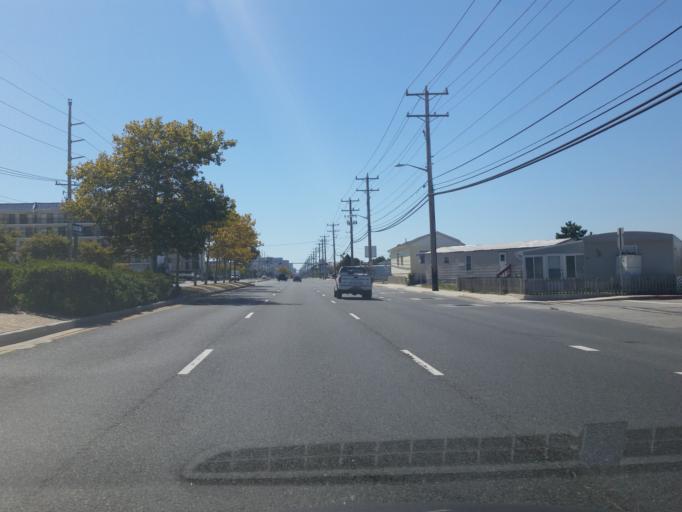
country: US
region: Delaware
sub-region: Sussex County
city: Bethany Beach
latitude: 38.4408
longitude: -75.0536
